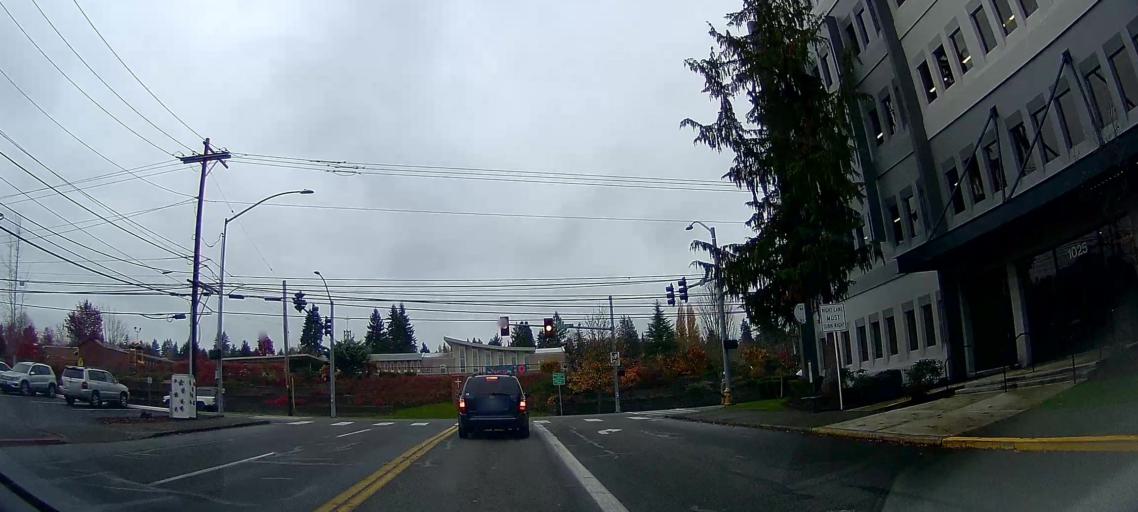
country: US
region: Washington
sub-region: Thurston County
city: Olympia
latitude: 47.0398
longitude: -122.8881
